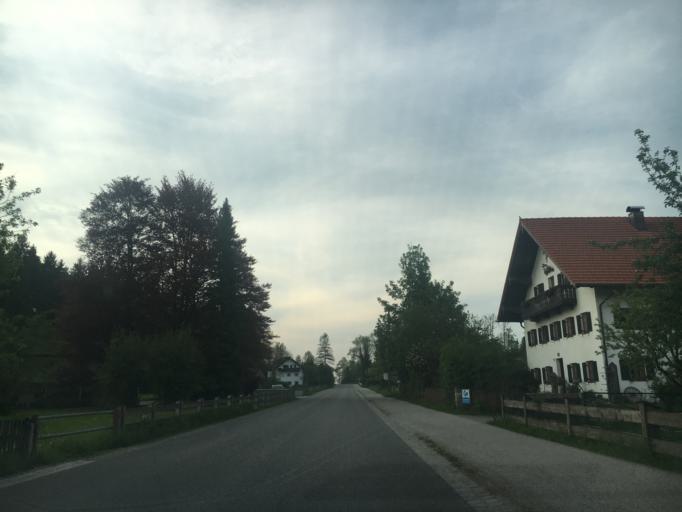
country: DE
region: Bavaria
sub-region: Upper Bavaria
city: Benediktbeuern
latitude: 47.6943
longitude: 11.4057
